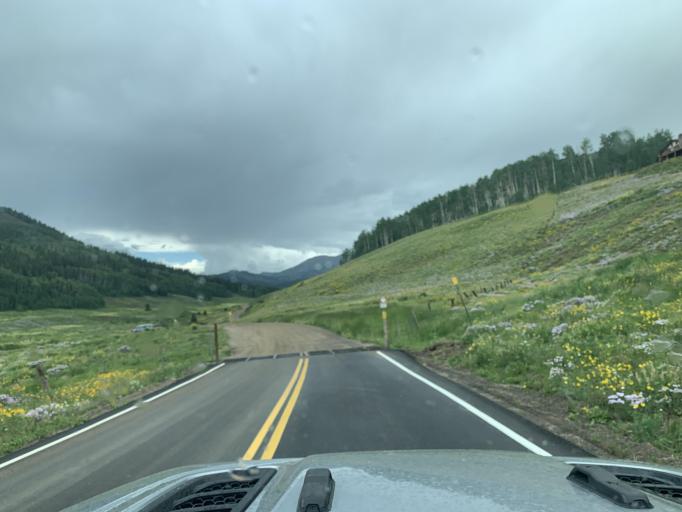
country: US
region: Colorado
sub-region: Gunnison County
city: Crested Butte
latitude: 38.9145
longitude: -107.0003
